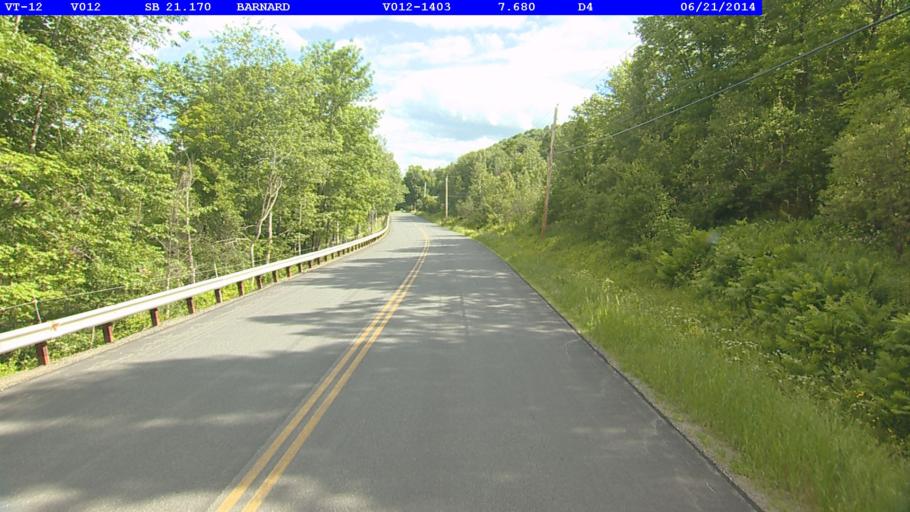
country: US
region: Vermont
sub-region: Orange County
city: Randolph
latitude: 43.7662
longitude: -72.6375
